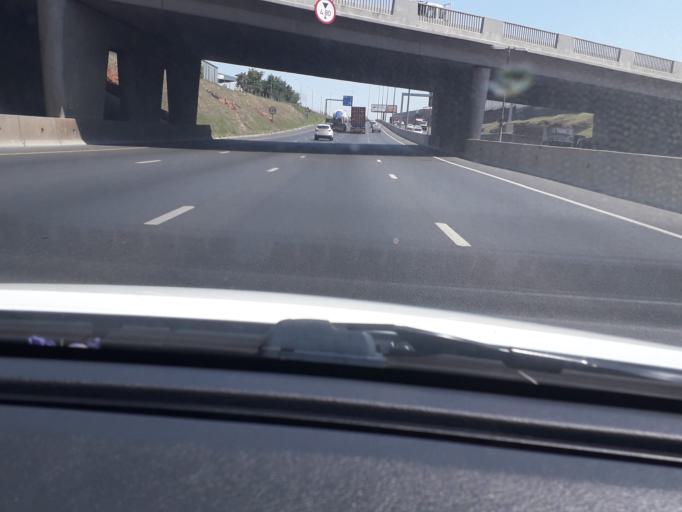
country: ZA
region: Gauteng
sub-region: Ekurhuleni Metropolitan Municipality
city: Germiston
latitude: -26.1712
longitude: 28.1924
